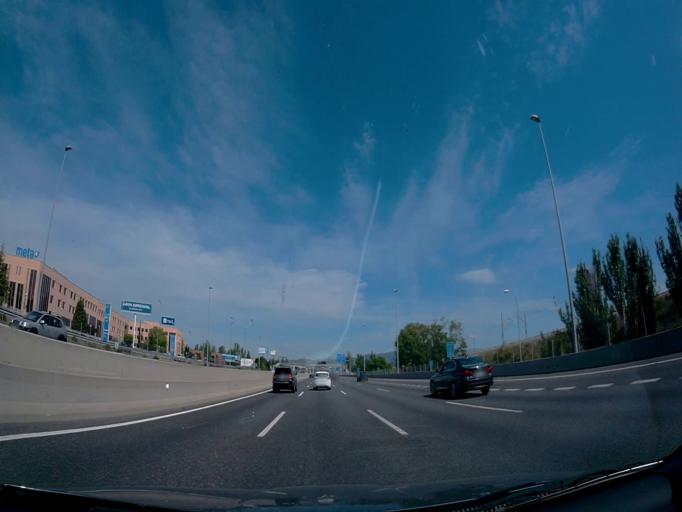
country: ES
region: Madrid
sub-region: Provincia de Madrid
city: Las Matas
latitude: 40.5388
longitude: -3.8904
